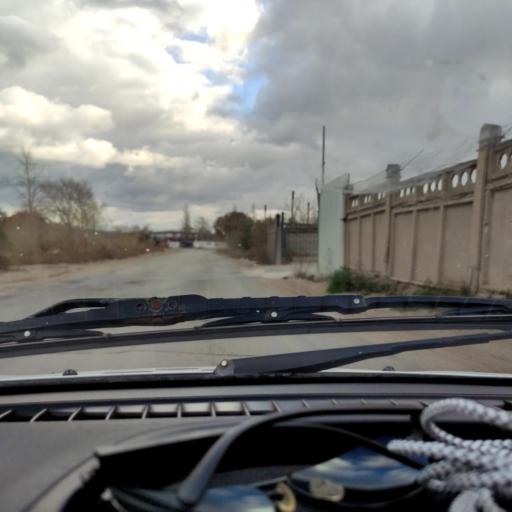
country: RU
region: Samara
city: Zhigulevsk
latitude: 53.4767
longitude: 49.4976
